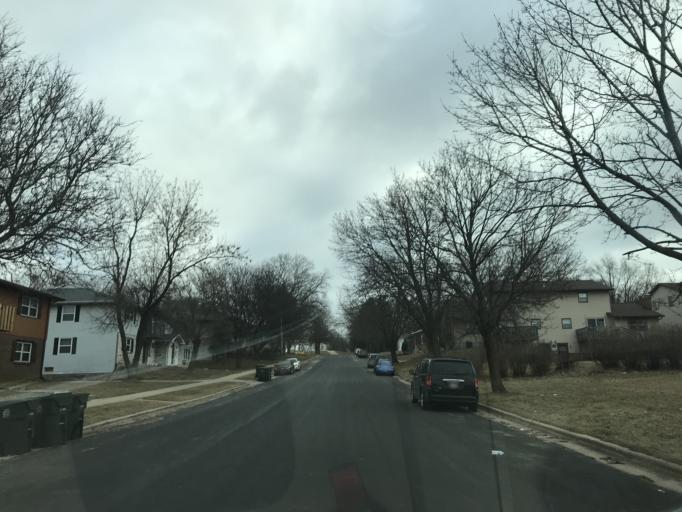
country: US
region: Wisconsin
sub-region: Dane County
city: Monona
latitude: 43.1102
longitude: -89.3084
